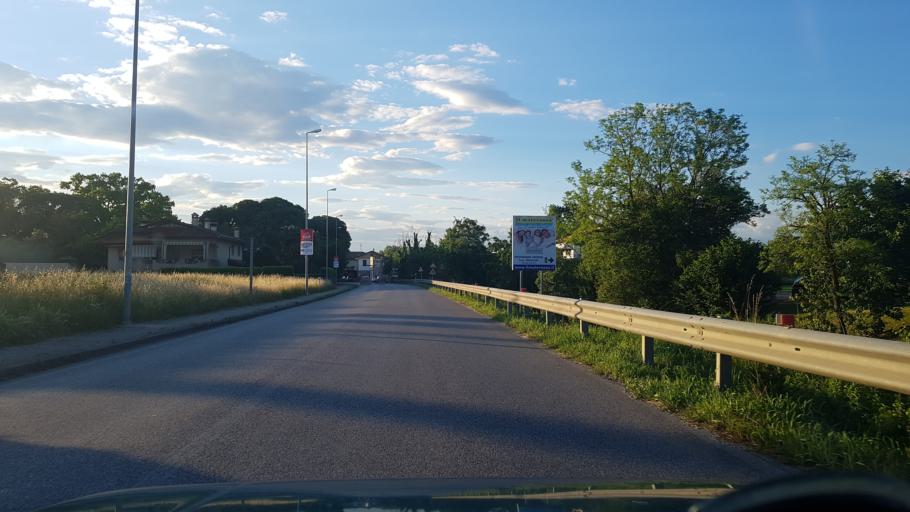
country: IT
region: Friuli Venezia Giulia
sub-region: Provincia di Udine
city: Santa Maria la Longa
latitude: 45.9311
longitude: 13.2924
